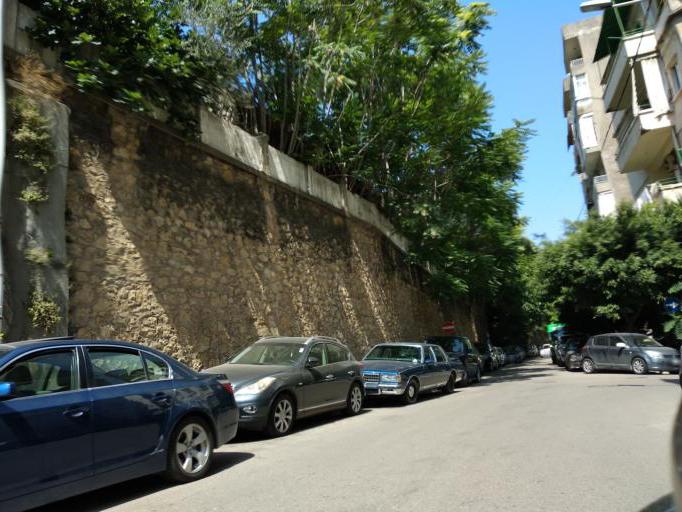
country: LB
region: Mont-Liban
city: Jdaidet el Matn
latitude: 33.8954
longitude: 35.5309
